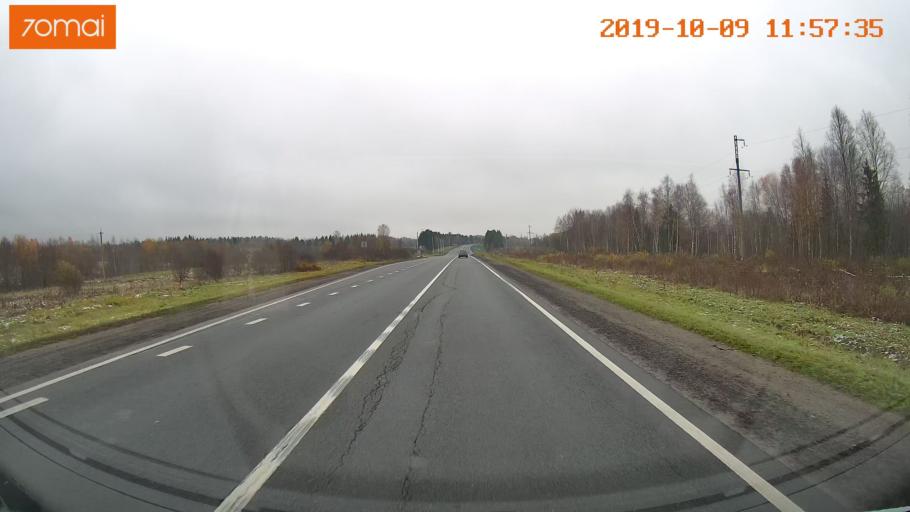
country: RU
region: Vologda
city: Gryazovets
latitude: 58.7303
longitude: 40.2934
